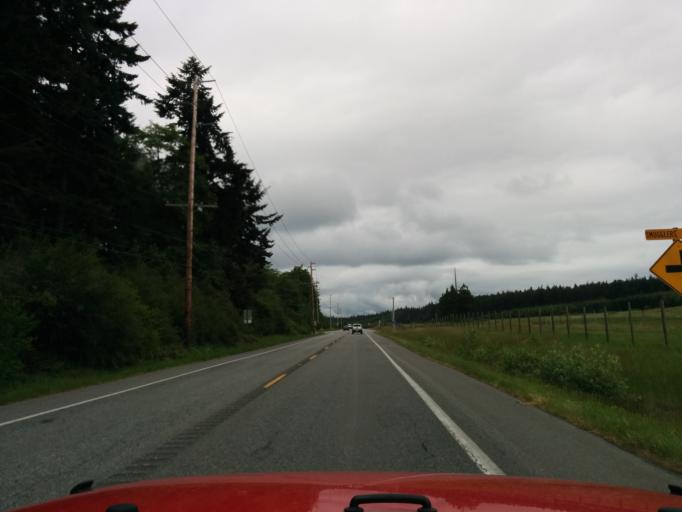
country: US
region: Washington
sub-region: Island County
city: Camano
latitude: 48.1067
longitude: -122.5792
